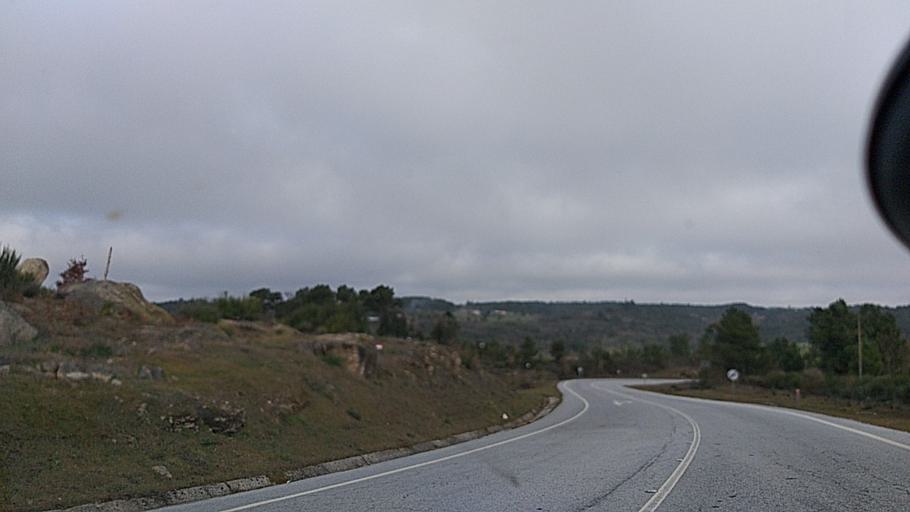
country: PT
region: Guarda
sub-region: Aguiar da Beira
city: Aguiar da Beira
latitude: 40.7739
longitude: -7.5049
